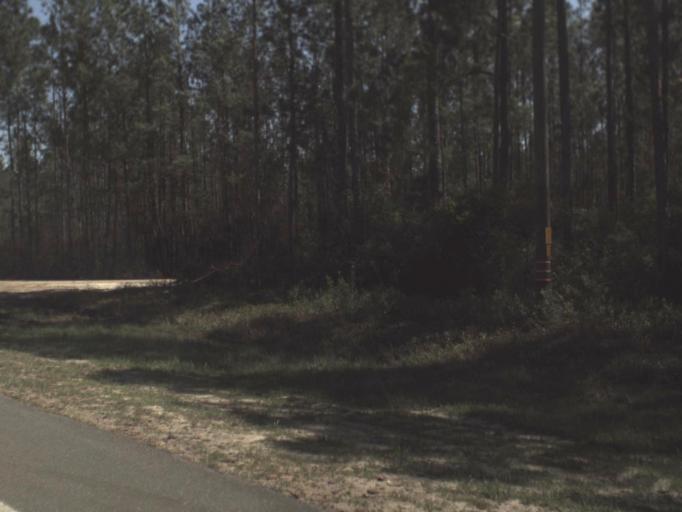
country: US
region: Florida
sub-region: Liberty County
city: Bristol
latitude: 30.4077
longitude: -84.8356
